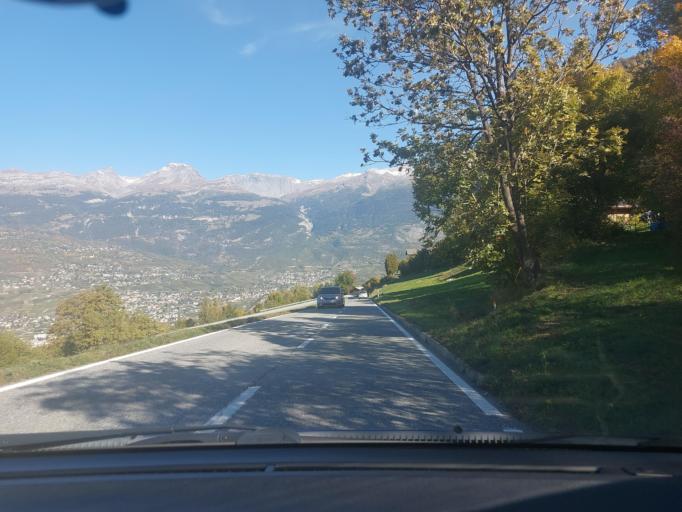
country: CH
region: Valais
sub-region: Sierre District
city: Chippis
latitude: 46.2735
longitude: 7.5495
